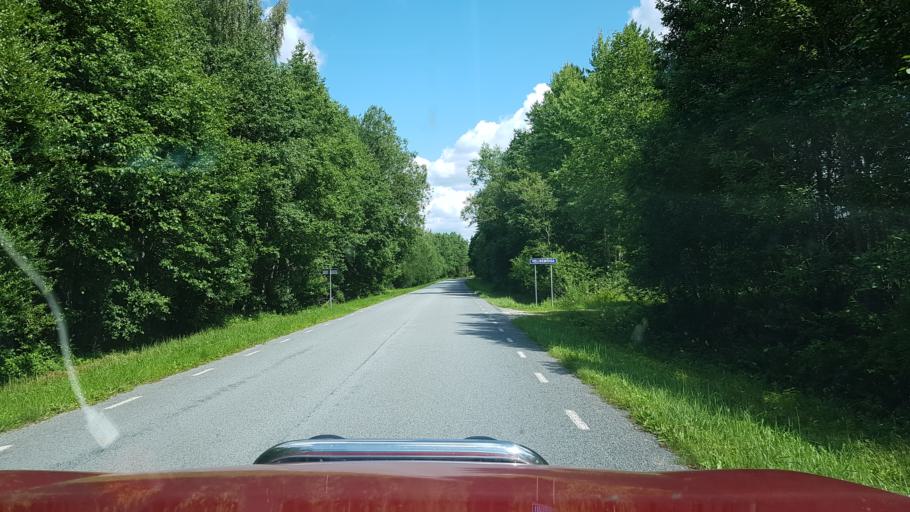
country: EE
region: Raplamaa
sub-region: Maerjamaa vald
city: Marjamaa
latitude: 58.7672
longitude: 24.4354
